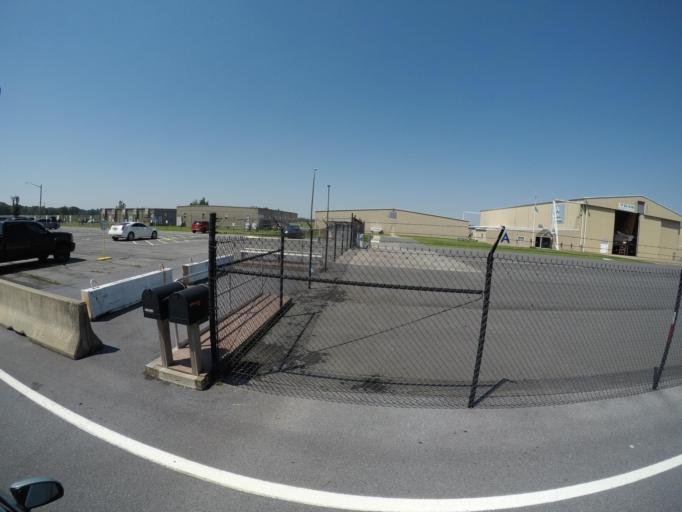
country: US
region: Delaware
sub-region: Sussex County
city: Georgetown
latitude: 38.6905
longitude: -75.3533
